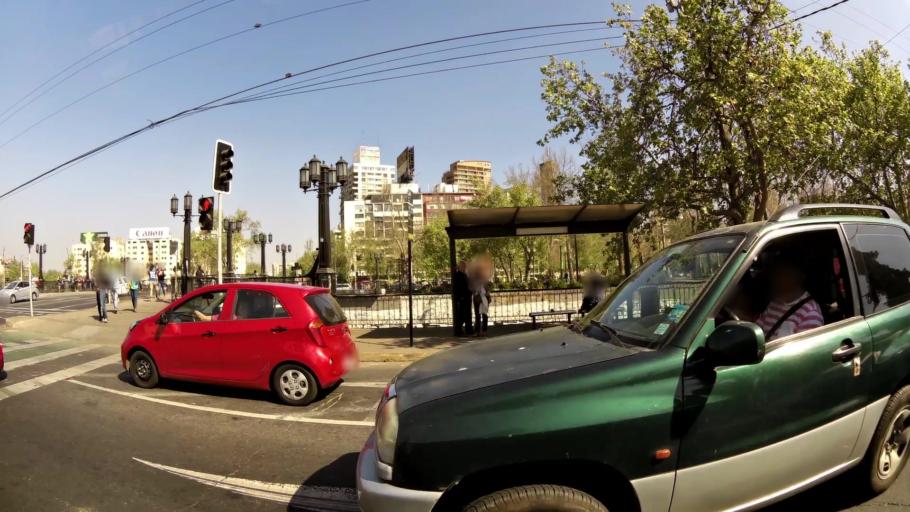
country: CL
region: Santiago Metropolitan
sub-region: Provincia de Santiago
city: Santiago
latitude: -33.4357
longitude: -70.6355
